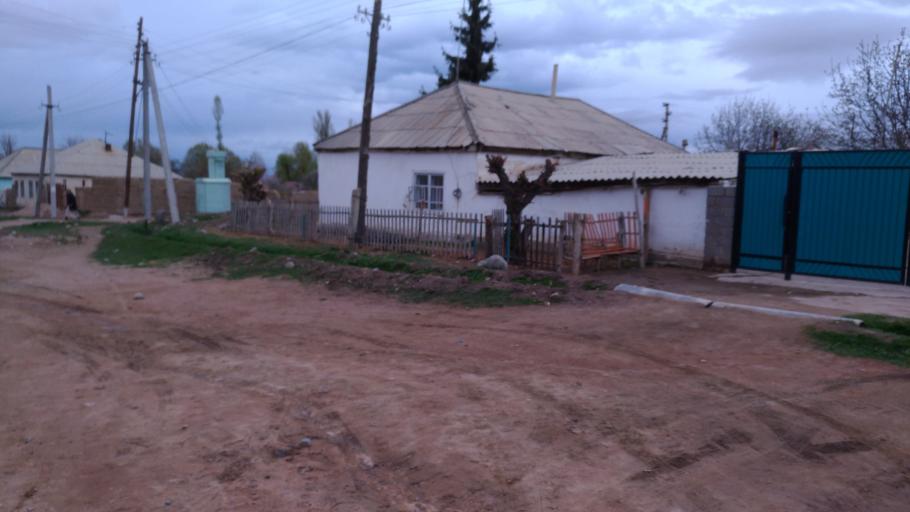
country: KG
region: Ysyk-Koel
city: Bokombayevskoye
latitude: 42.1139
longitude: 76.9836
